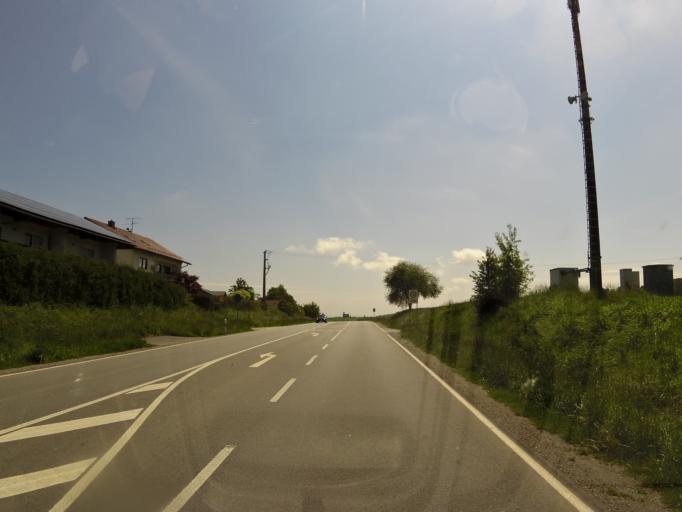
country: DE
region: Bavaria
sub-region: Lower Bavaria
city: Aicha vorm Wald
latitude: 48.6667
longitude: 13.2641
